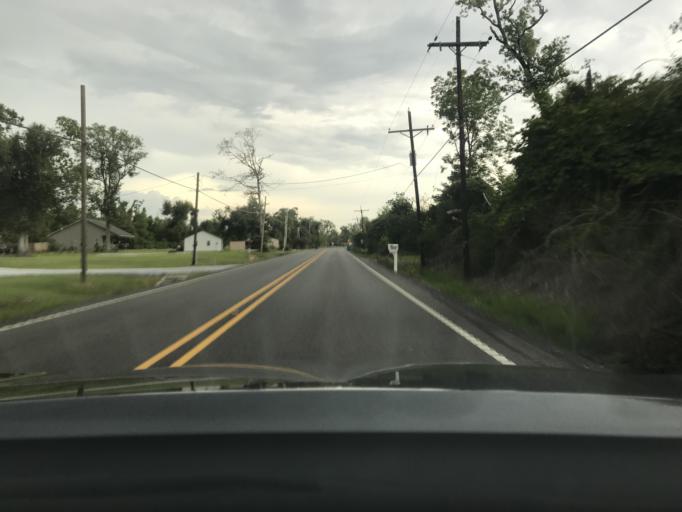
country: US
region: Louisiana
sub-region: Calcasieu Parish
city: Westlake
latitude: 30.2688
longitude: -93.2431
